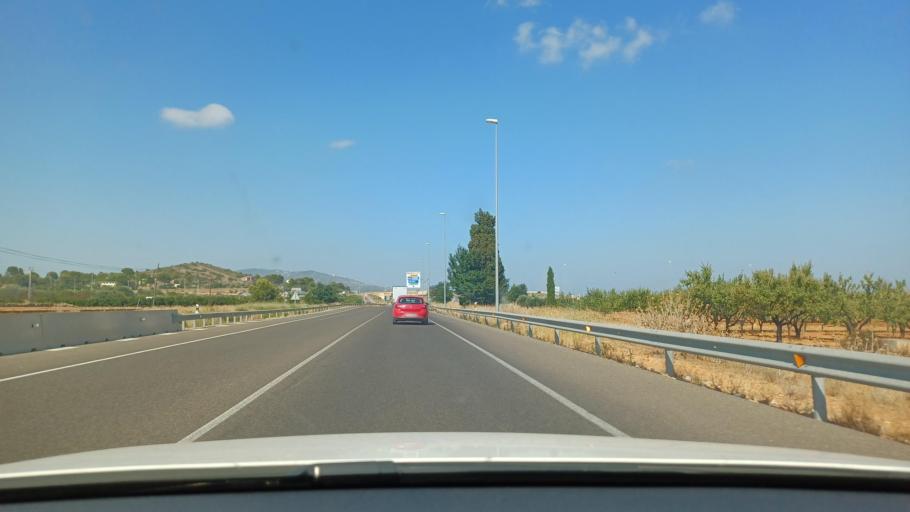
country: ES
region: Valencia
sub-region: Provincia de Castello
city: Torreblanca
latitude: 40.2246
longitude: 0.2071
